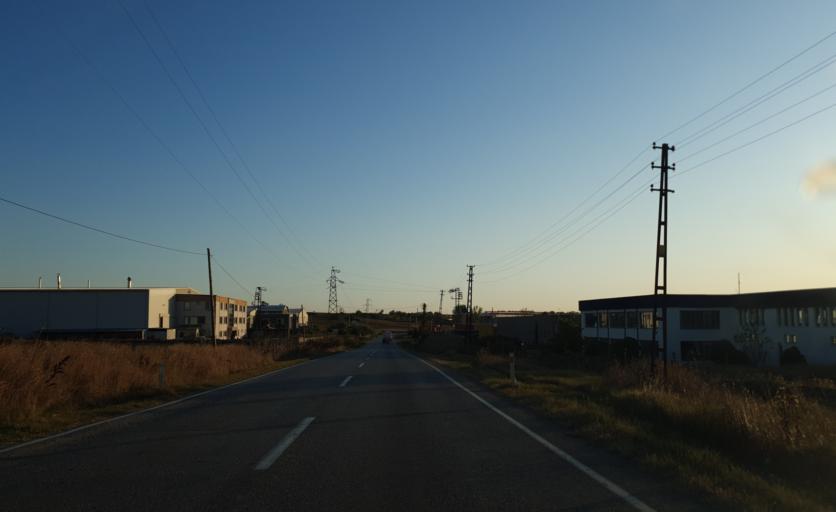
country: TR
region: Tekirdag
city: Beyazkoy
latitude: 41.3403
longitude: 27.7080
